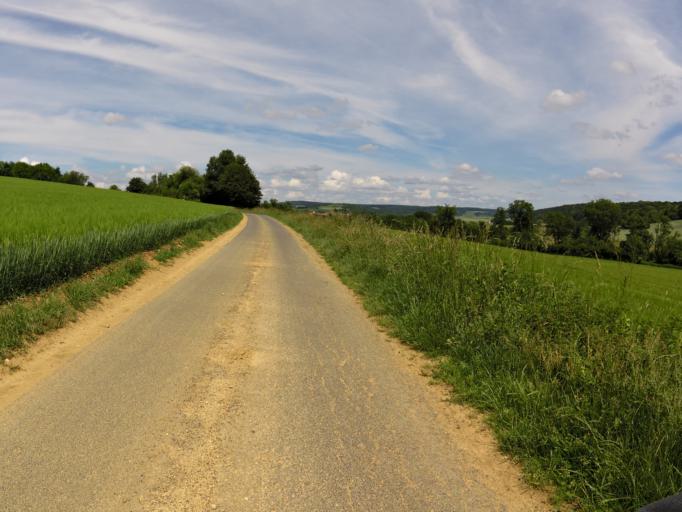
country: FR
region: Champagne-Ardenne
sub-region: Departement des Ardennes
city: Mouzon
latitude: 49.5279
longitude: 5.0919
